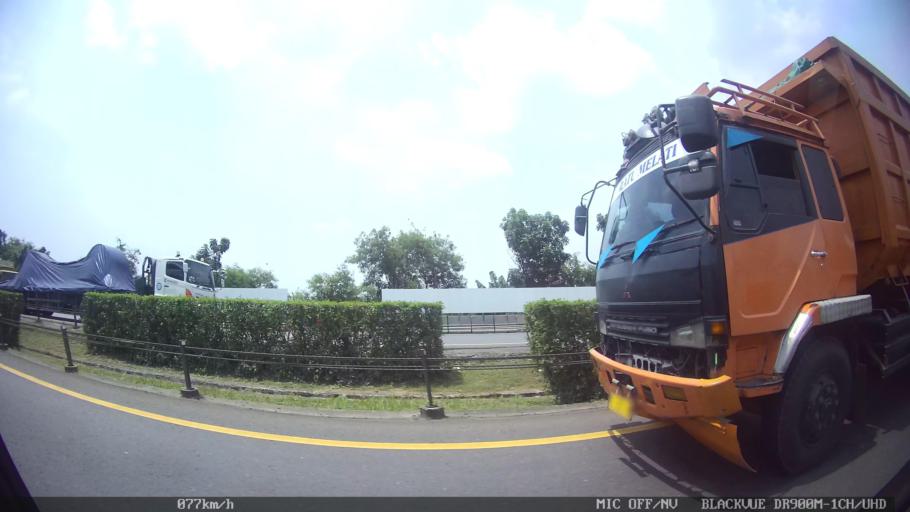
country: ID
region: West Java
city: Kresek
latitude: -6.1414
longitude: 106.2690
